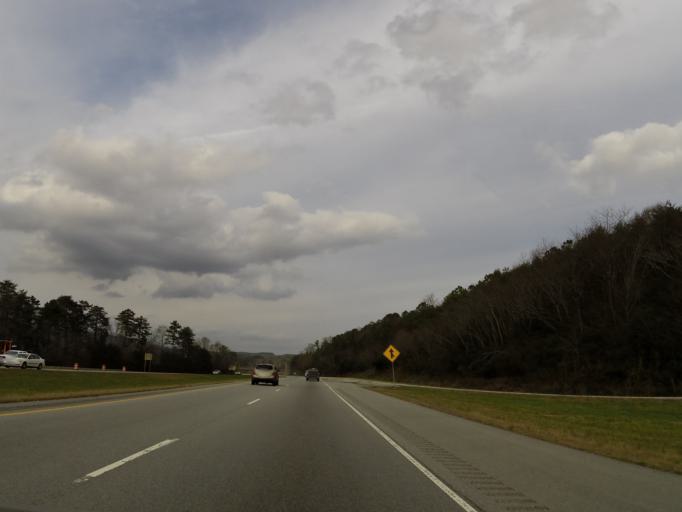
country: US
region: Tennessee
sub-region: Hamilton County
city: Soddy-Daisy
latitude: 35.2792
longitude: -85.1543
